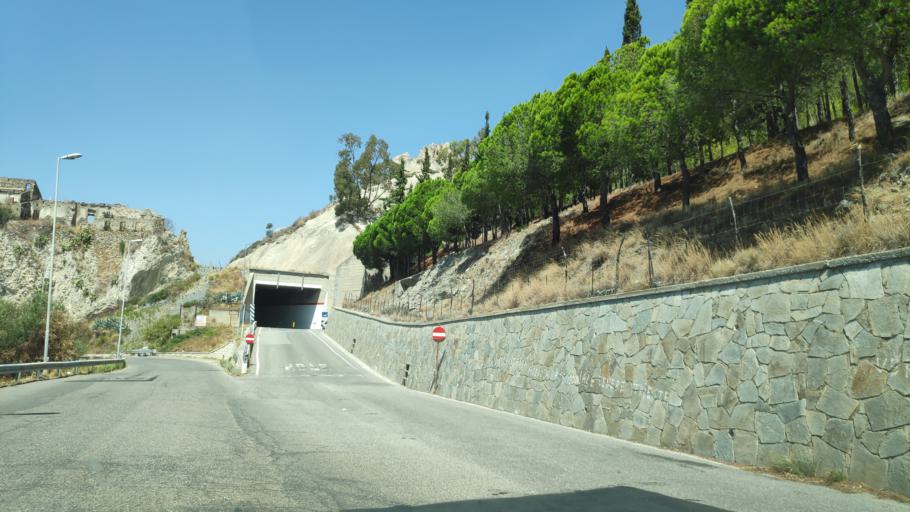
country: IT
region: Calabria
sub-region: Provincia di Reggio Calabria
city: Bova Marina
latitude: 37.9285
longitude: 15.9337
